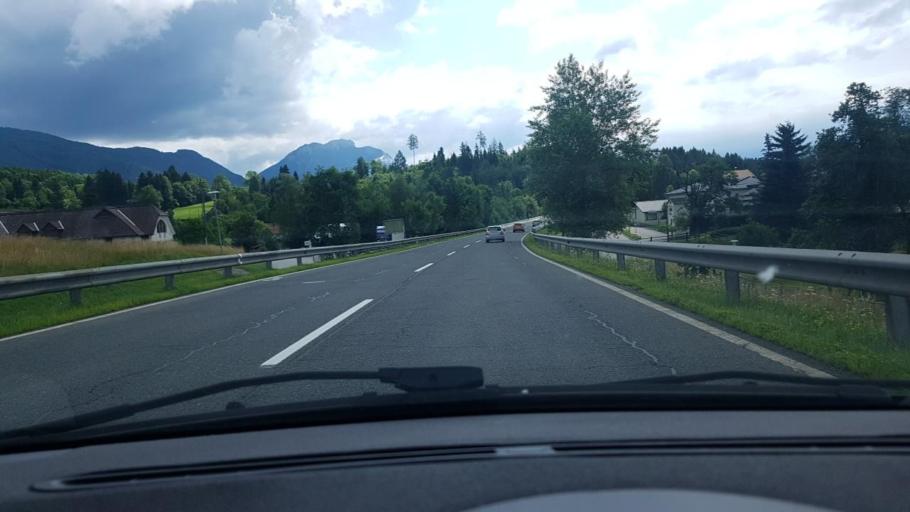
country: AT
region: Carinthia
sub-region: Politischer Bezirk Villach Land
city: Feistritz an der Gail
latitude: 46.6197
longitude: 13.5187
